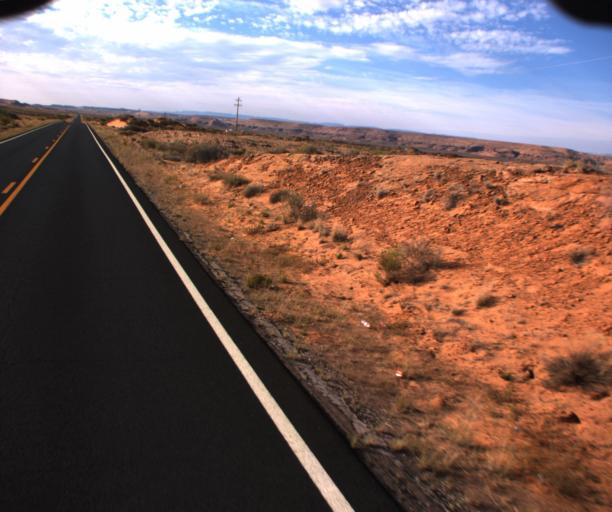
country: US
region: Arizona
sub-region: Apache County
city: Many Farms
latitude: 36.8149
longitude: -109.6464
